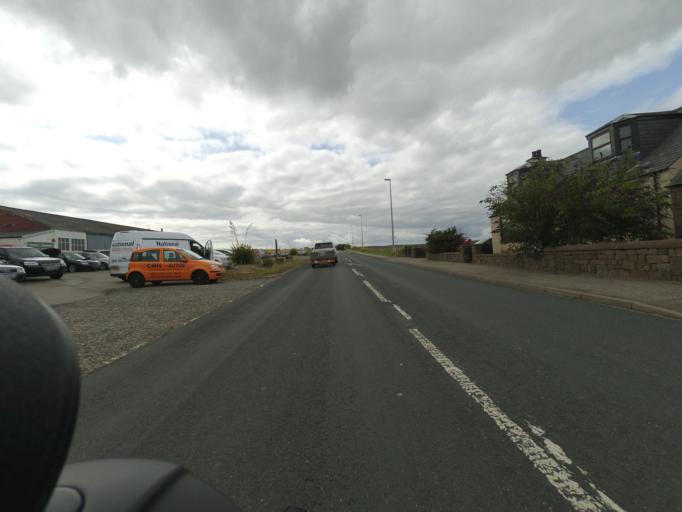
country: GB
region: Scotland
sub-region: Aberdeenshire
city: Laurencekirk
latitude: 56.7717
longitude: -2.4243
